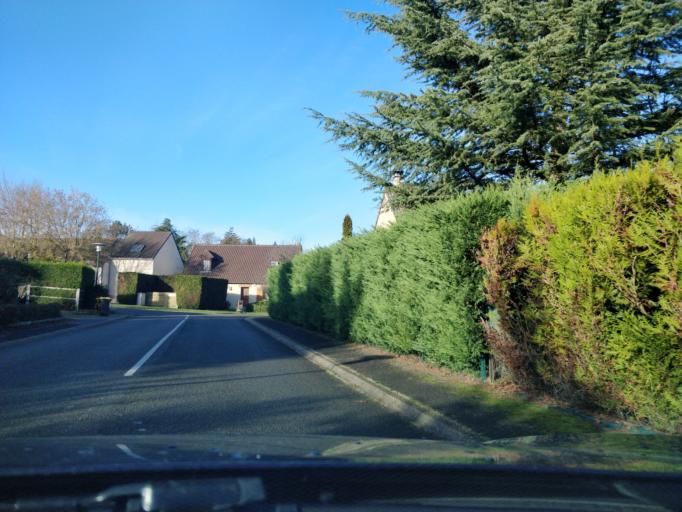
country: FR
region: Ile-de-France
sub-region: Departement de l'Essonne
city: Limours
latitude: 48.6401
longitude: 2.0898
